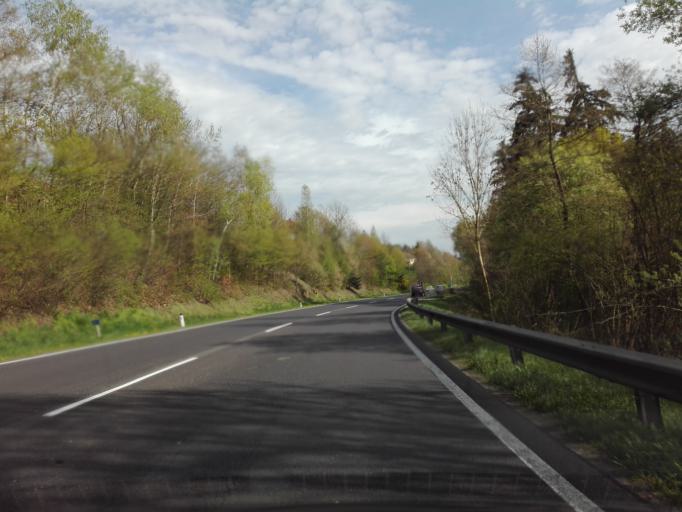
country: AT
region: Upper Austria
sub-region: Politischer Bezirk Urfahr-Umgebung
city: Herzogsdorf
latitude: 48.4033
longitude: 14.0721
